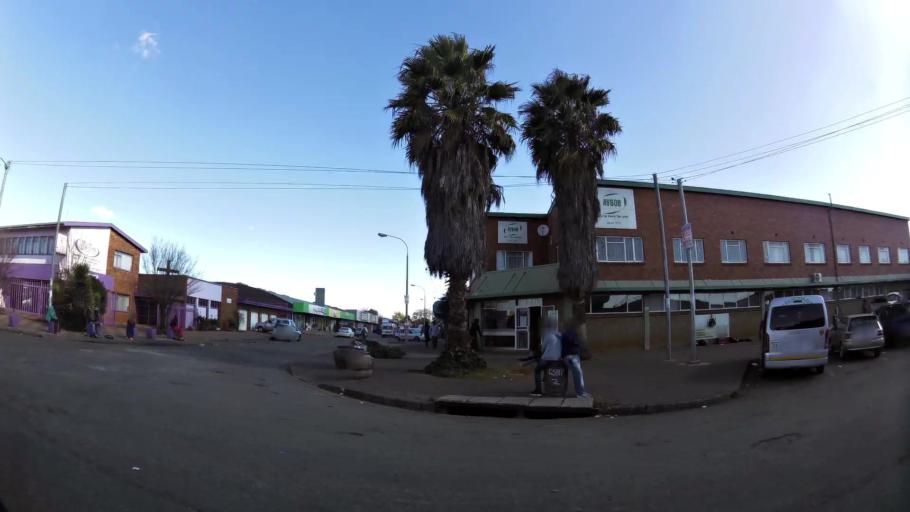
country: ZA
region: Gauteng
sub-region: West Rand District Municipality
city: Carletonville
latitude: -26.3536
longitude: 27.3961
